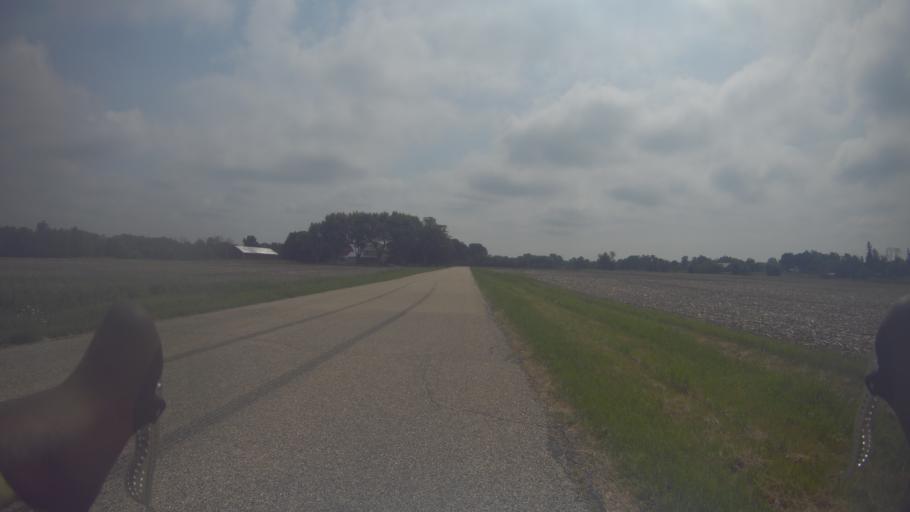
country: US
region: Wisconsin
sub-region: Jefferson County
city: Cambridge
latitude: 42.9202
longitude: -89.0362
